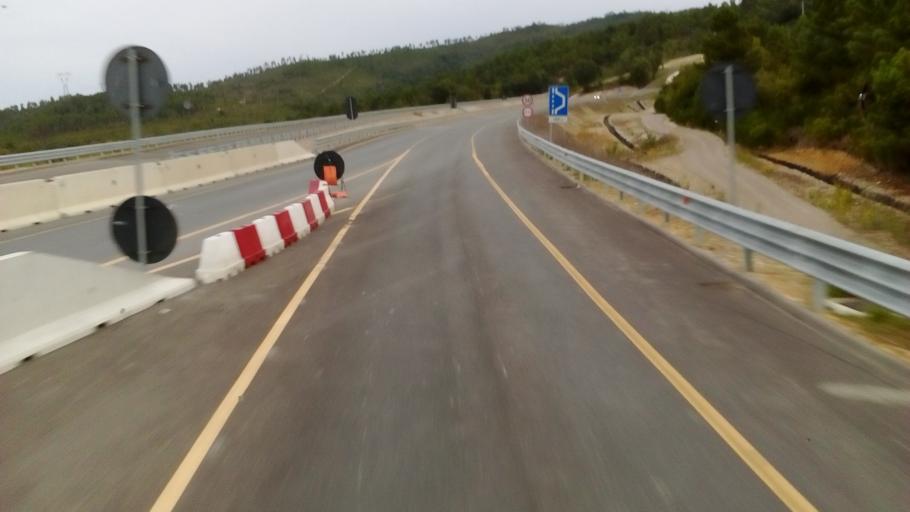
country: IT
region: Tuscany
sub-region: Provincia di Grosseto
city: Civitella Marittima
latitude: 43.0322
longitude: 11.2764
